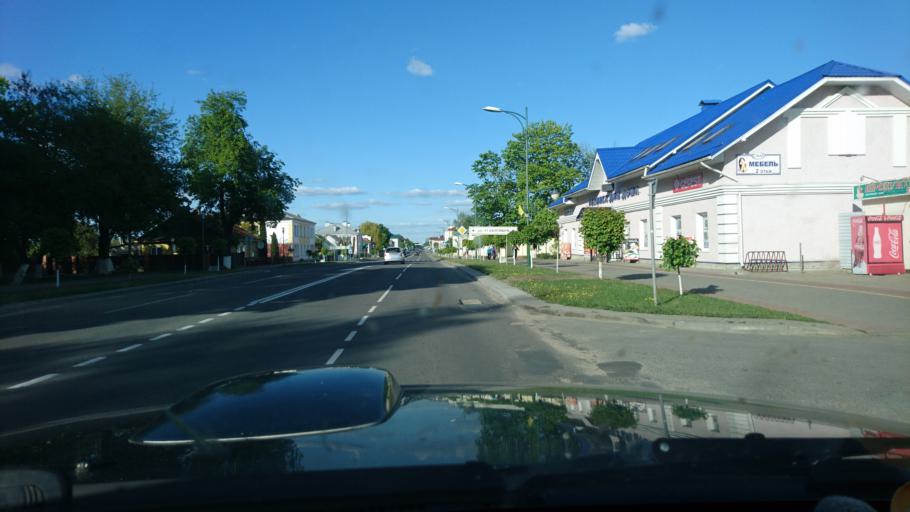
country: BY
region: Brest
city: Byaroza
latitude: 52.5306
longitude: 24.9771
